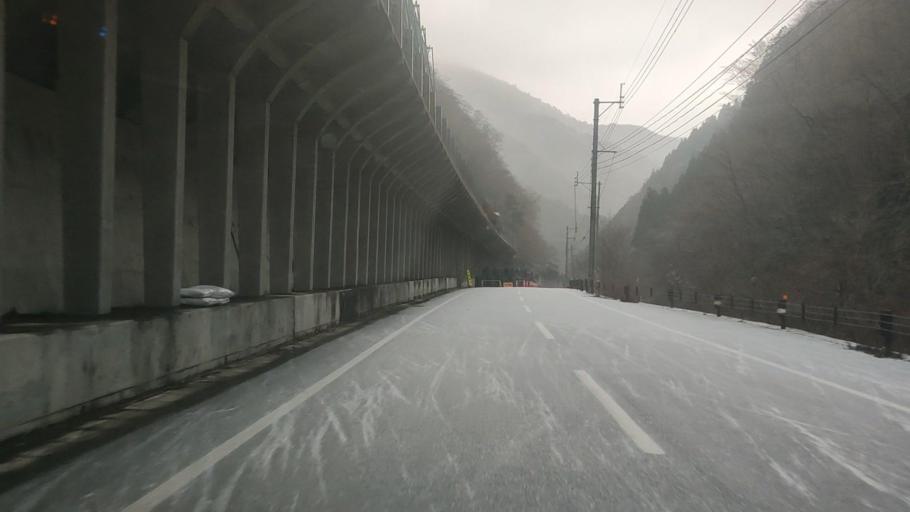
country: JP
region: Kumamoto
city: Matsubase
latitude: 32.5547
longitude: 130.9263
